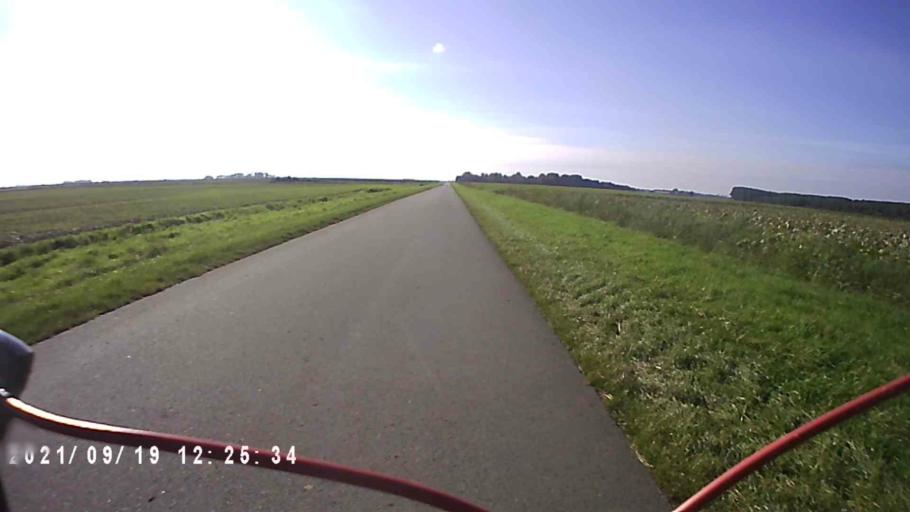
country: NL
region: Groningen
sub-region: Gemeente Slochteren
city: Slochteren
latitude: 53.2368
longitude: 6.8917
